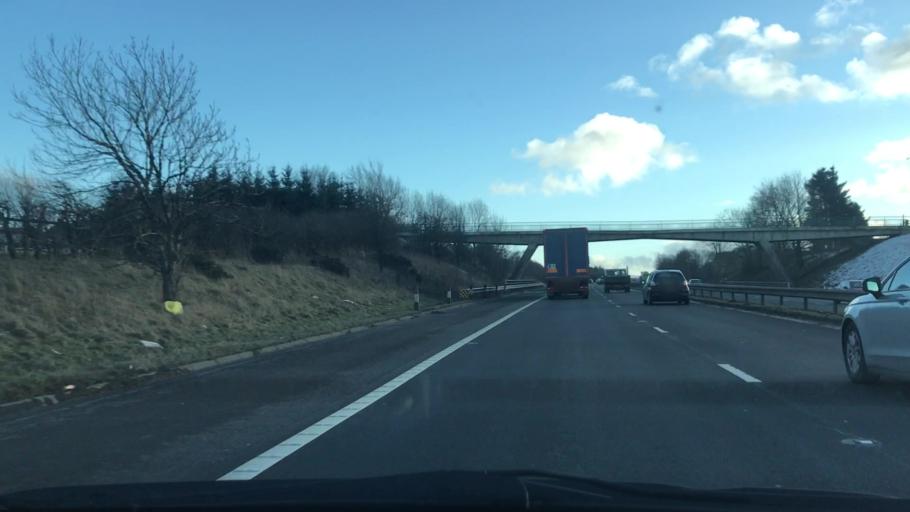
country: GB
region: Scotland
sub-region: South Lanarkshire
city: Larkhall
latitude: 55.6983
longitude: -3.9459
